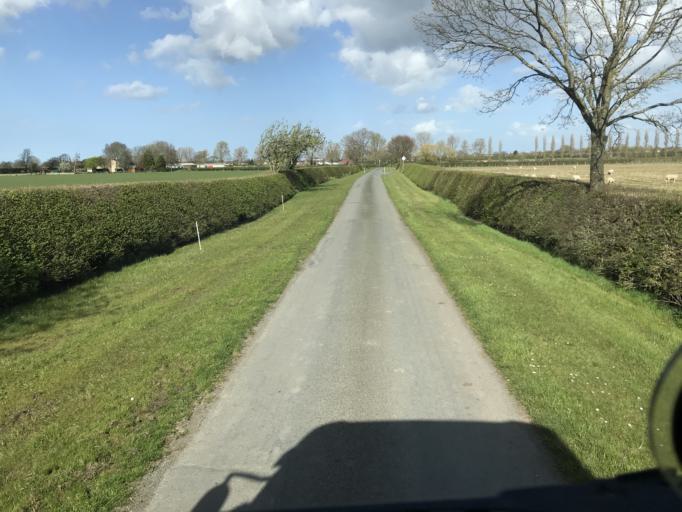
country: GB
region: England
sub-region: Cheshire West and Chester
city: Blacon
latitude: 53.1688
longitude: -2.9487
